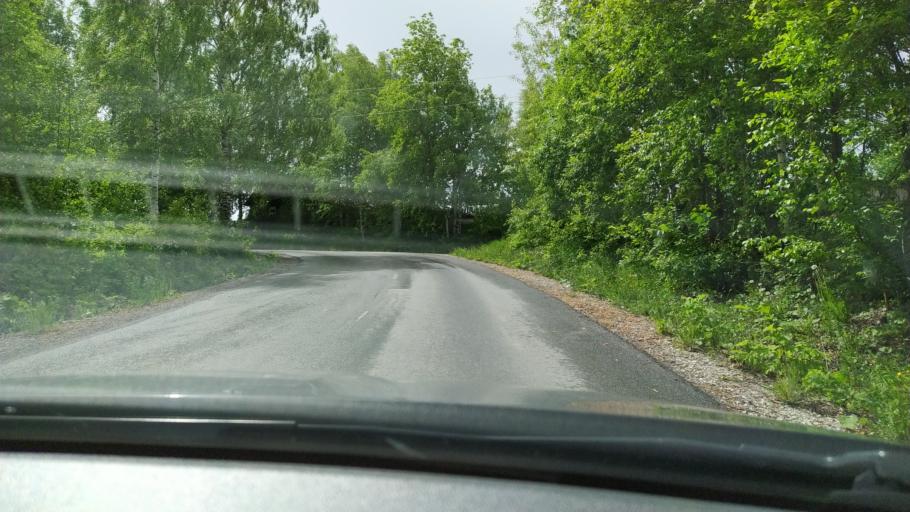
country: RU
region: Perm
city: Gremyachinsk
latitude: 58.5129
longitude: 57.8345
